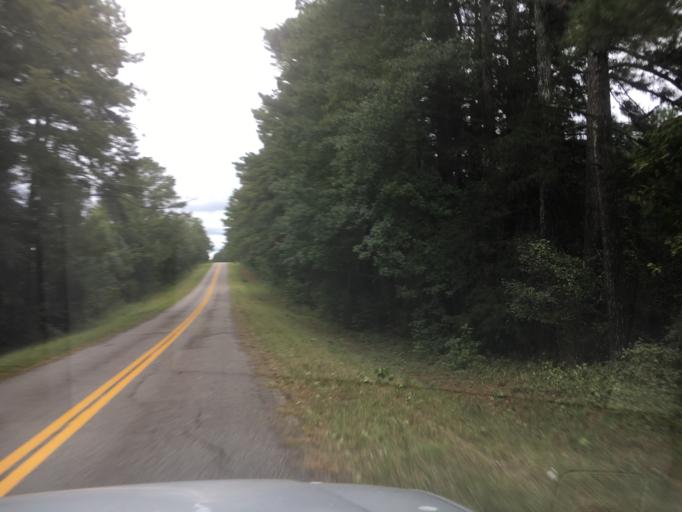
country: US
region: Georgia
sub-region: Wilkes County
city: Washington
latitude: 33.6939
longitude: -82.5986
